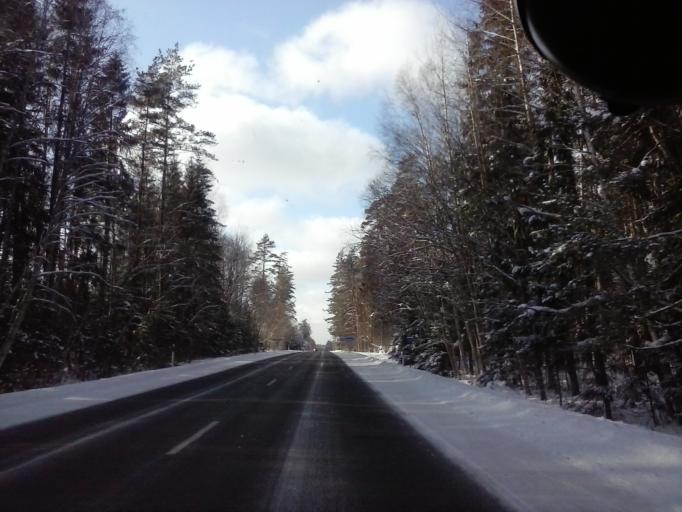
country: EE
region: Viljandimaa
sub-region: Moisakuela linn
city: Moisakula
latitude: 58.2503
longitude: 25.1845
